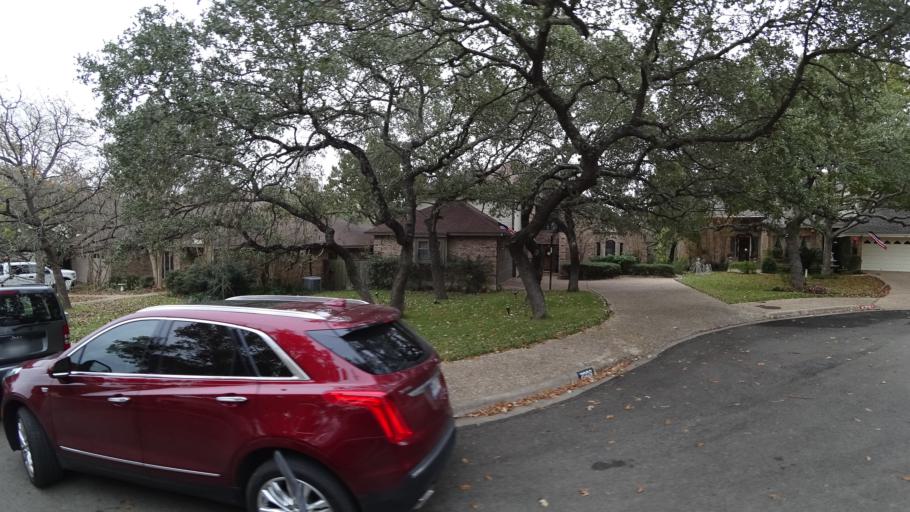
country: US
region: Texas
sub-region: Williamson County
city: Jollyville
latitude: 30.3761
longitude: -97.7965
